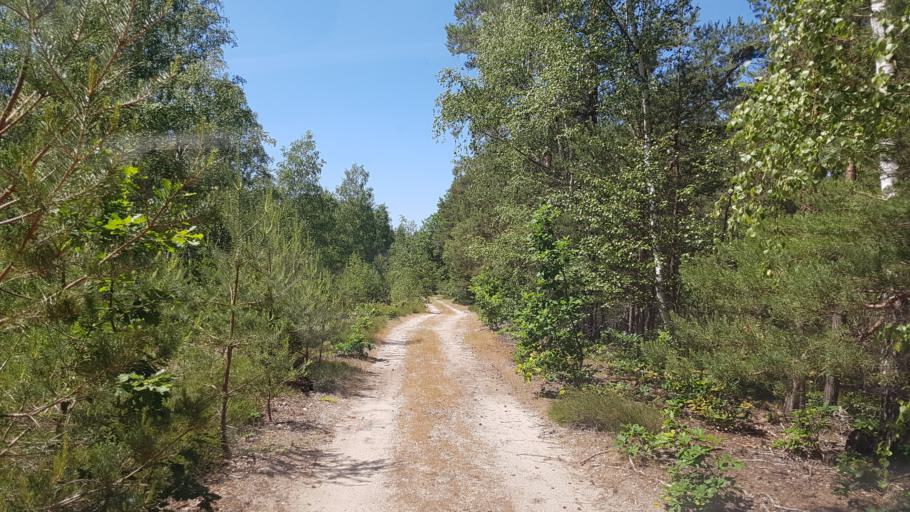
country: DE
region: Brandenburg
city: Ruckersdorf
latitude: 51.5454
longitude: 13.5428
